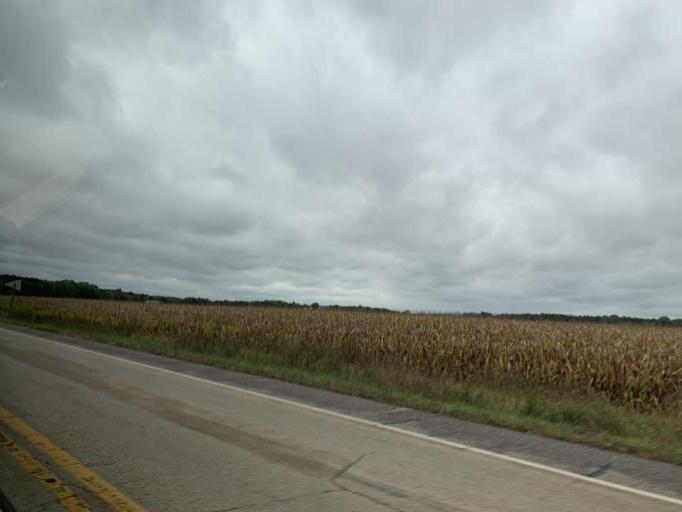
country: US
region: Wisconsin
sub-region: Sauk County
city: Sauk City
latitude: 43.2674
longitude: -89.7982
